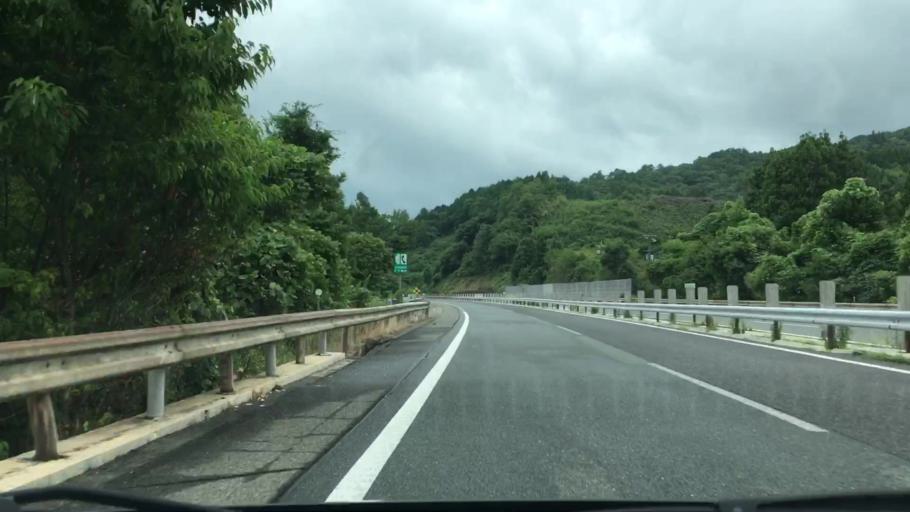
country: JP
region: Okayama
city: Niimi
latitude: 34.9413
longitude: 133.3283
